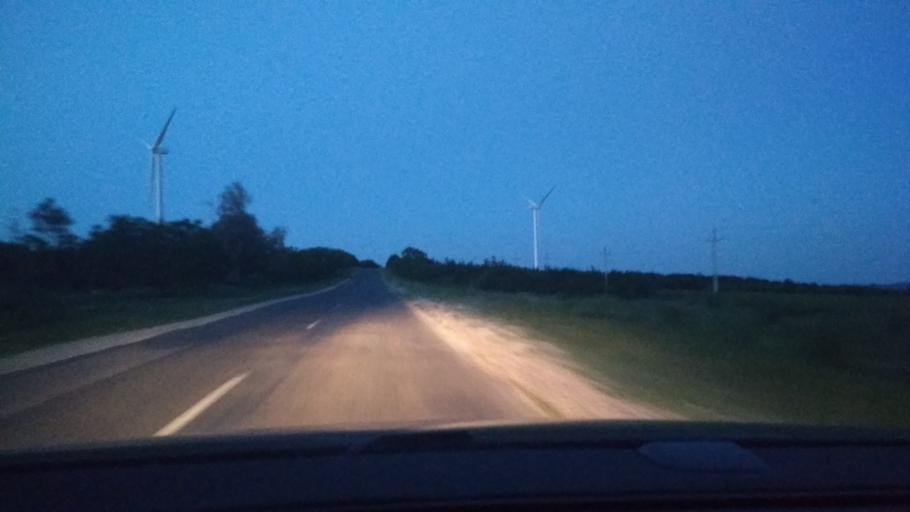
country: MD
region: Nisporeni
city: Nisporeni
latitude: 47.1552
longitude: 28.2005
